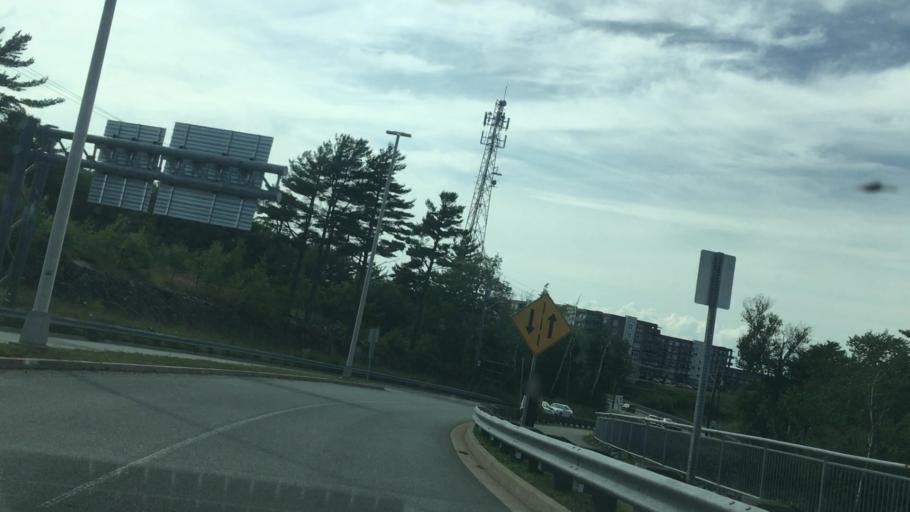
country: CA
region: Nova Scotia
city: Dartmouth
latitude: 44.6983
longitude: -63.6936
